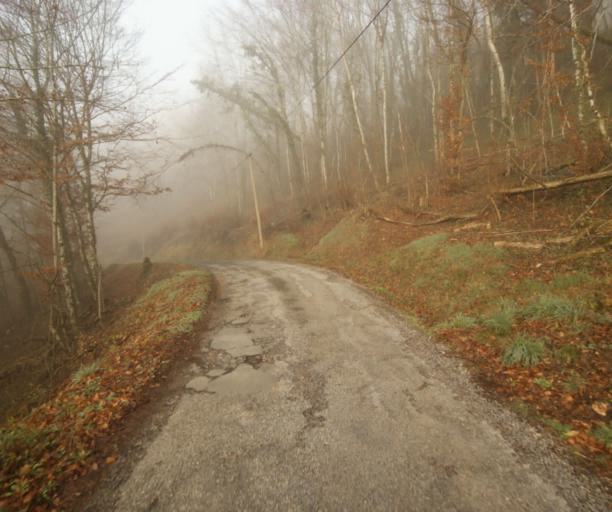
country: FR
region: Limousin
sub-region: Departement de la Correze
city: Laguenne
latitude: 45.2619
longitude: 1.7861
